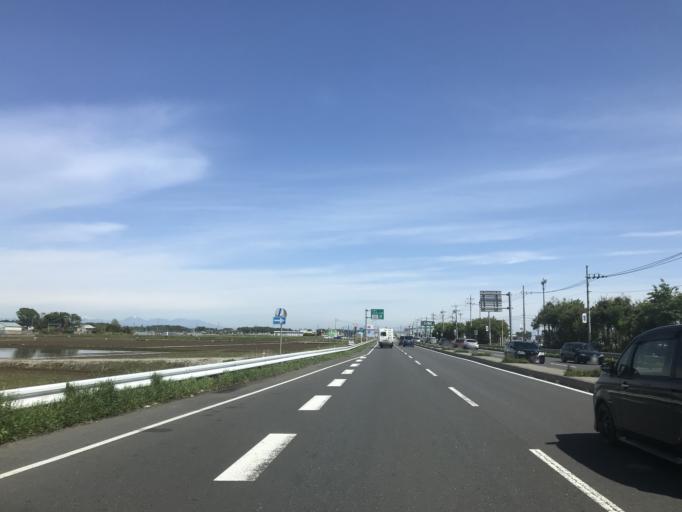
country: JP
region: Ibaraki
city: Ishige
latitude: 36.1901
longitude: 139.9879
